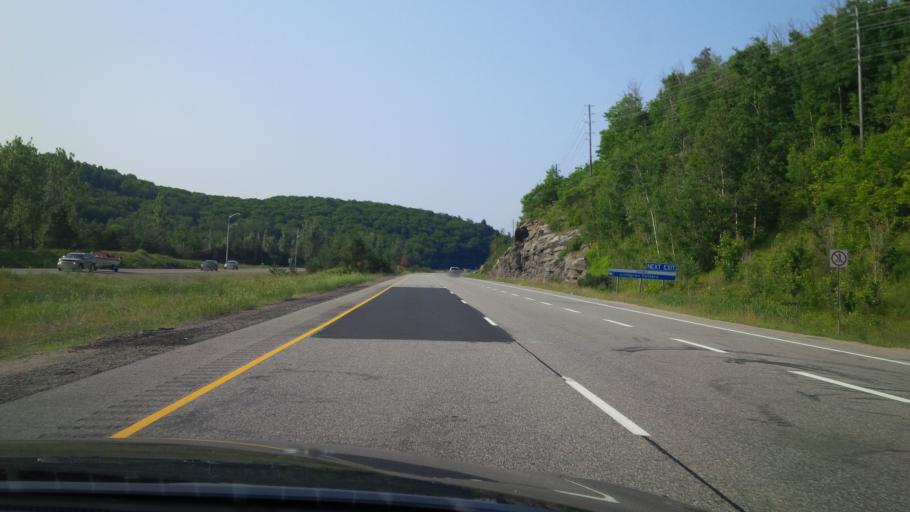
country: CA
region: Ontario
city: Huntsville
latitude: 45.3122
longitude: -79.2458
